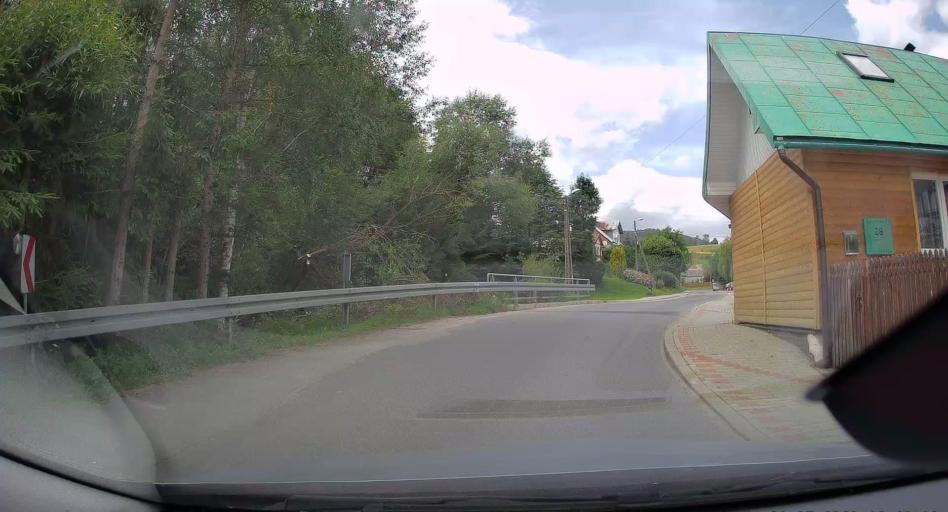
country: PL
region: Lesser Poland Voivodeship
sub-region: Powiat nowosadecki
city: Muszyna
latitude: 49.3721
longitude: 20.8884
